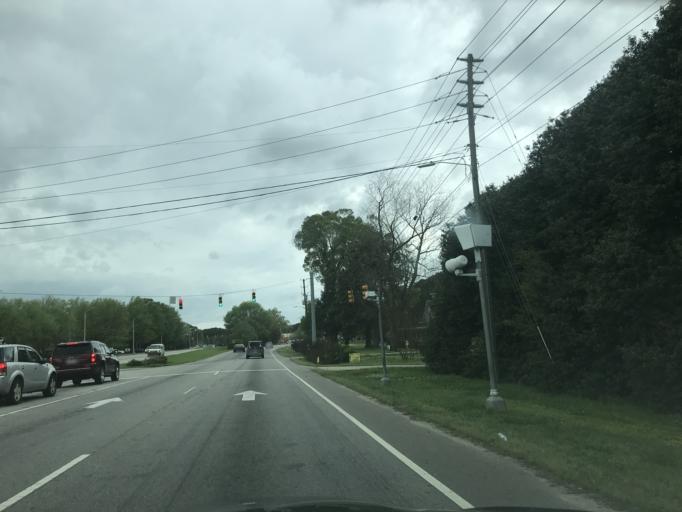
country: US
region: North Carolina
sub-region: Wake County
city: Knightdale
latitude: 35.7985
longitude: -78.4916
